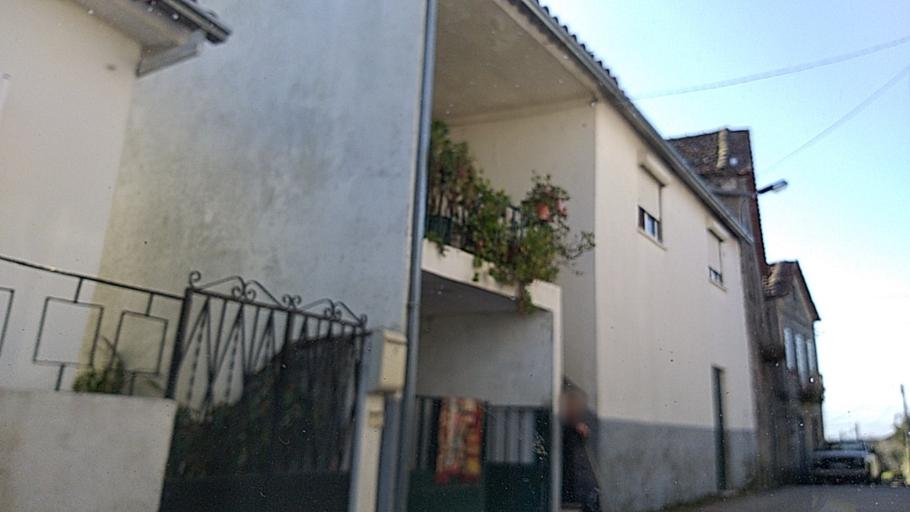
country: PT
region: Guarda
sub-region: Celorico da Beira
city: Celorico da Beira
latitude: 40.6761
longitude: -7.3970
